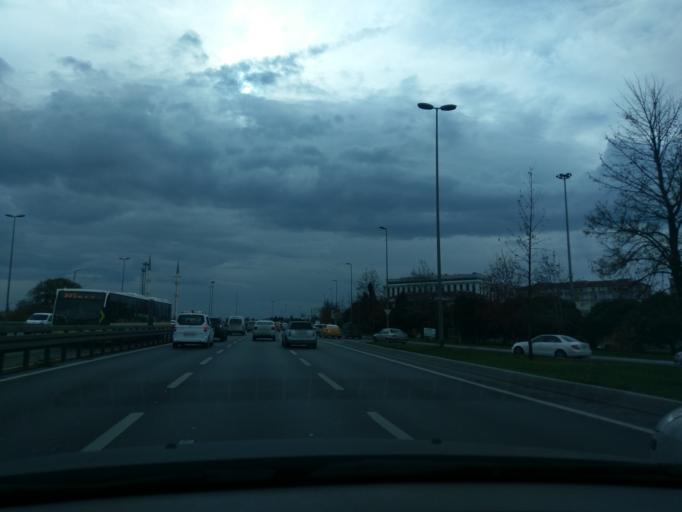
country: TR
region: Istanbul
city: Bahcelievler
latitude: 40.9911
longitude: 28.7936
